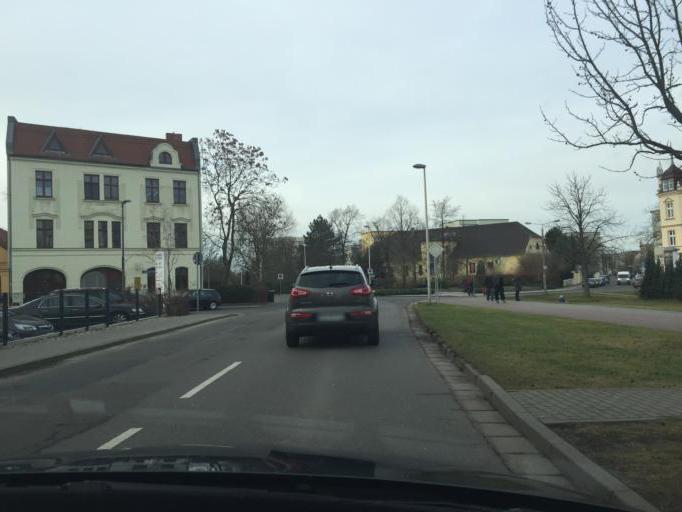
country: DE
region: Brandenburg
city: Cottbus
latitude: 51.7627
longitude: 14.3265
